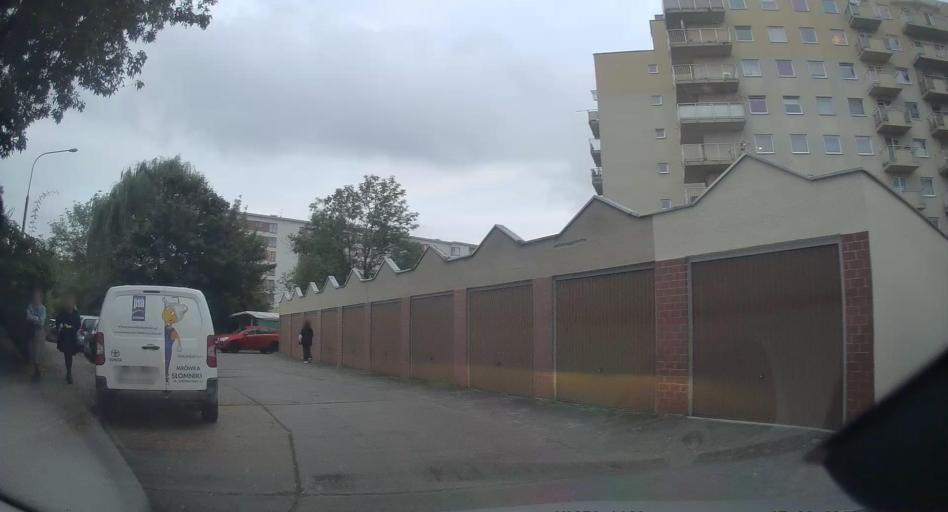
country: PL
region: Lesser Poland Voivodeship
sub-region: Krakow
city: Krakow
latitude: 50.0738
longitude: 19.9769
